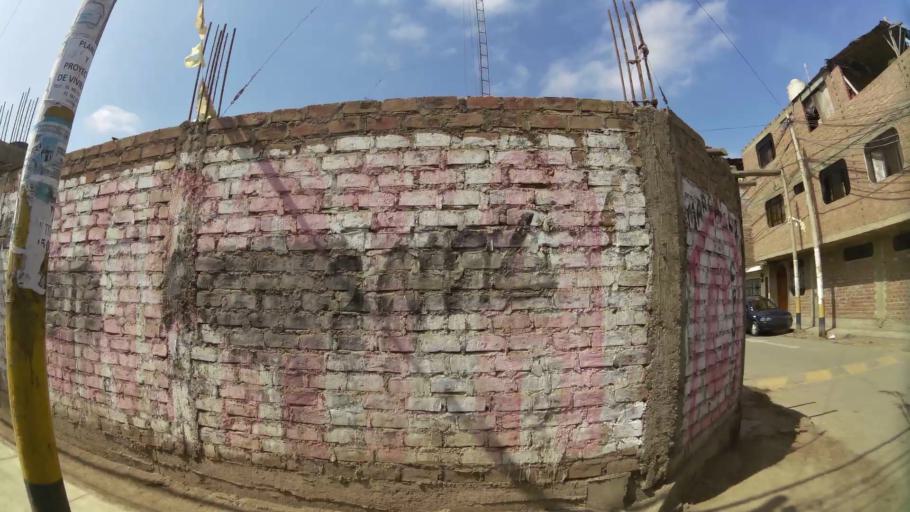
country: PE
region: Lima
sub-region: Provincia de Canete
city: Mala
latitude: -12.6567
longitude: -76.6328
